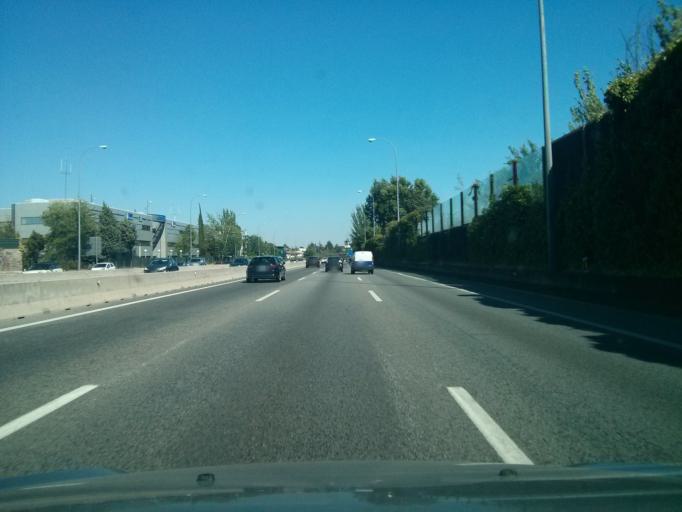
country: ES
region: Madrid
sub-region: Provincia de Madrid
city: Pozuelo de Alarcon
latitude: 40.4726
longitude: -3.8251
